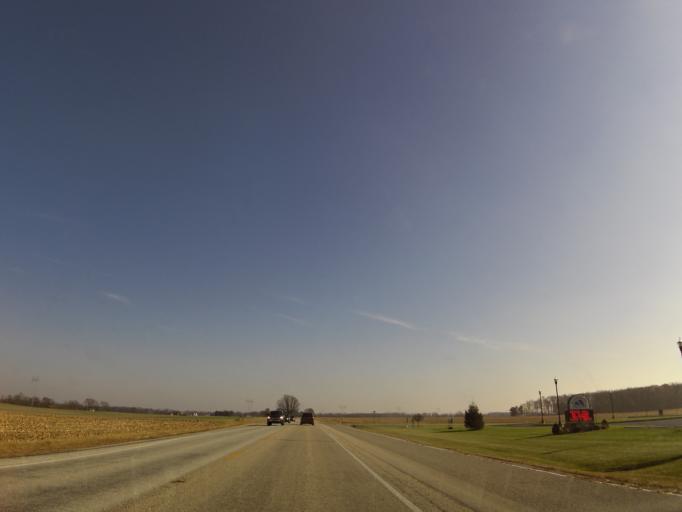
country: US
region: Indiana
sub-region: Shelby County
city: Morristown
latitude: 39.5730
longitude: -85.6045
